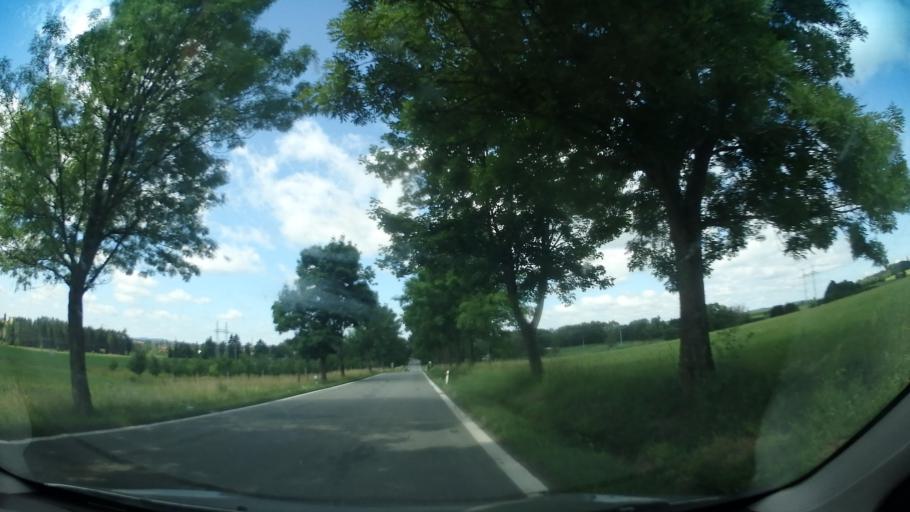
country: CZ
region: Vysocina
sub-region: Okres Zd'ar nad Sazavou
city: Zd'ar nad Sazavou
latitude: 49.5737
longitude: 15.9586
